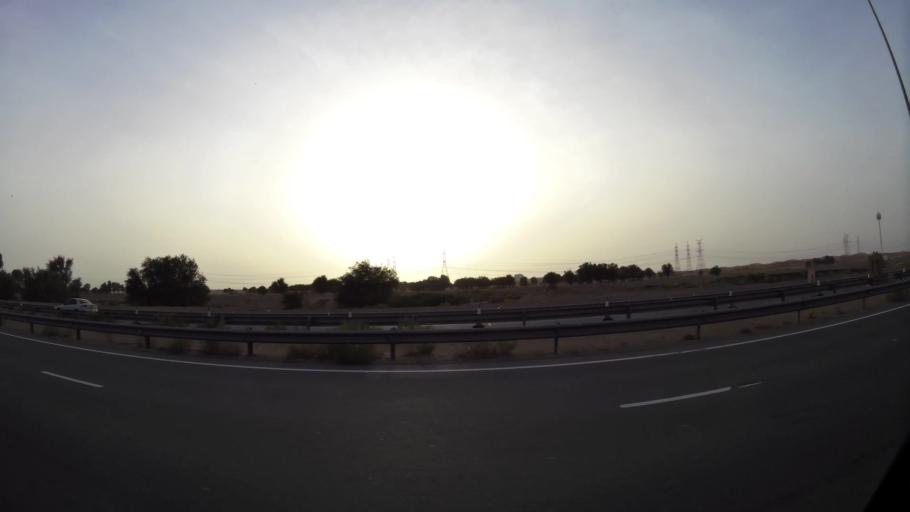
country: OM
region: Al Buraimi
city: Al Buraymi
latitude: 24.2835
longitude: 55.7328
